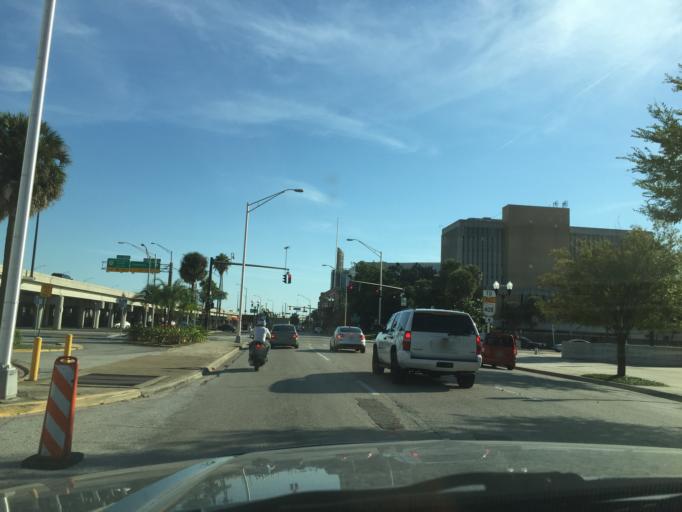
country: US
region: Florida
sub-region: Orange County
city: Orlando
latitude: 28.5426
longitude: -81.3829
